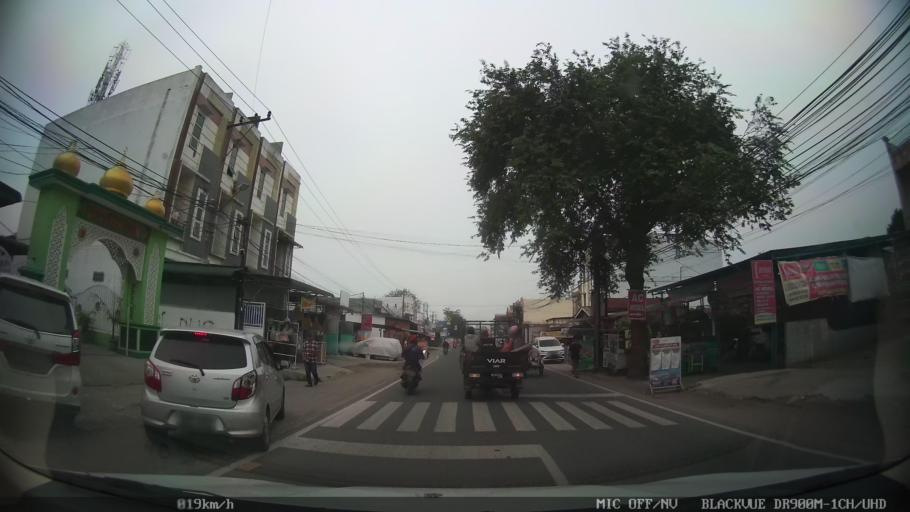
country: ID
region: North Sumatra
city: Medan
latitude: 3.5682
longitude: 98.7181
